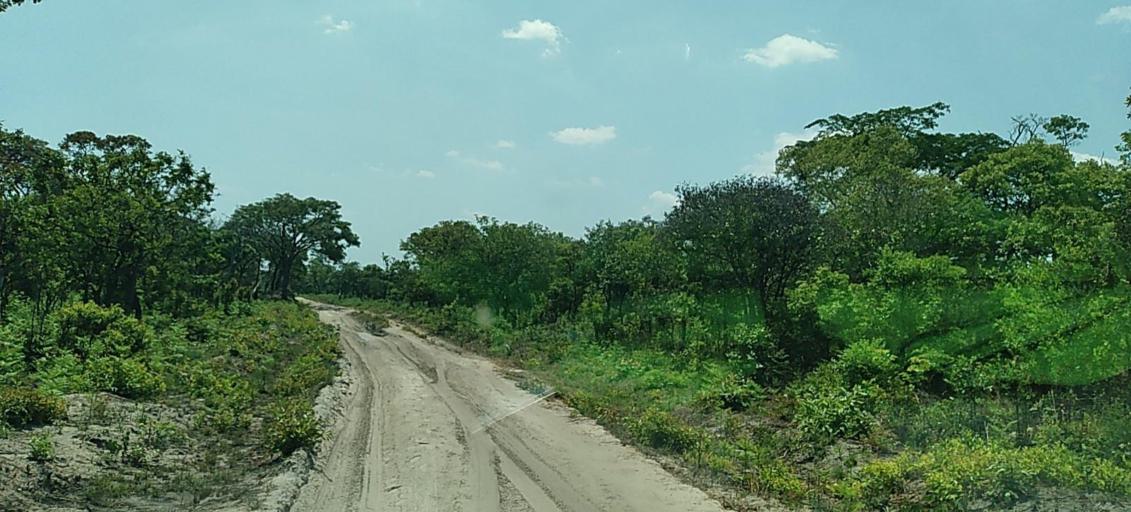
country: CD
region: Katanga
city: Kolwezi
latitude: -11.2990
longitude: 25.2271
